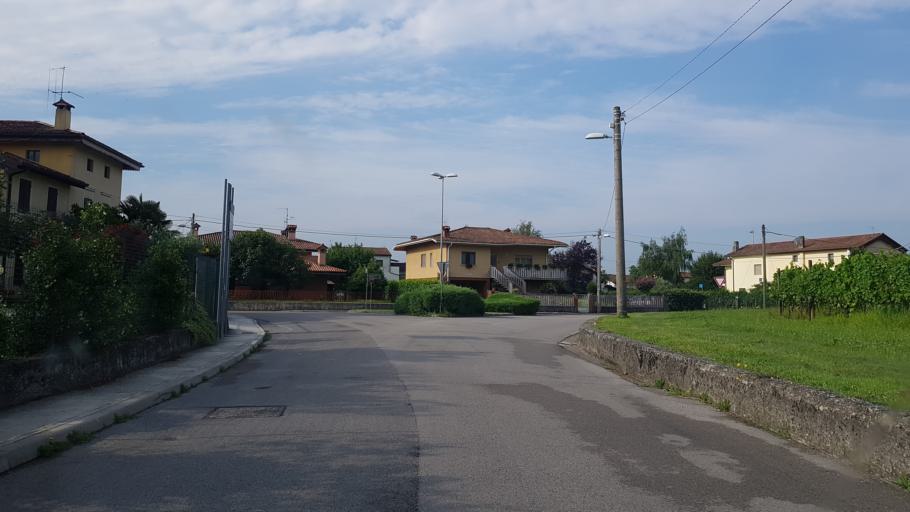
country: IT
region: Friuli Venezia Giulia
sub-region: Provincia di Gorizia
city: Mossa
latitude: 45.9397
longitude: 13.5463
